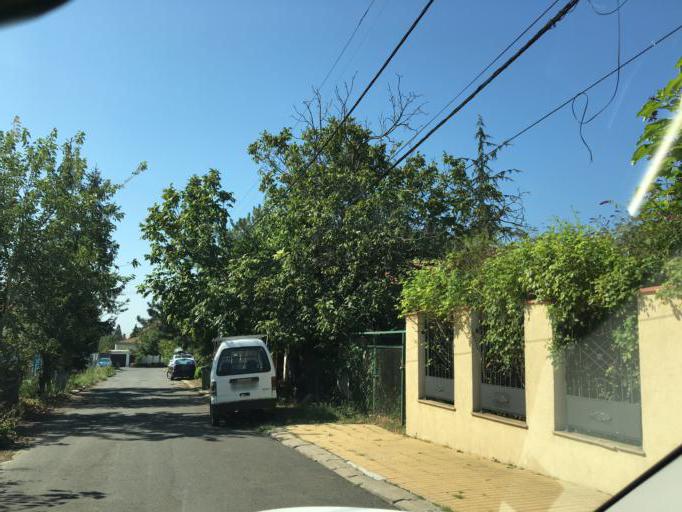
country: BG
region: Burgas
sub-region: Obshtina Kameno
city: Kameno
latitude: 42.6099
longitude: 27.3856
